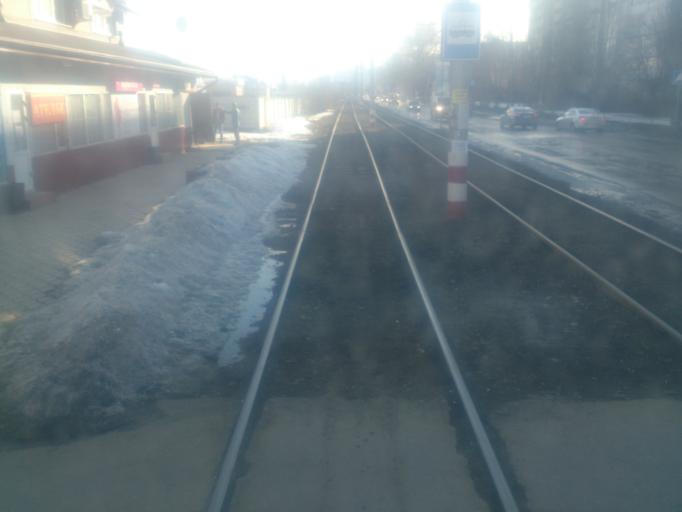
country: RU
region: Ulyanovsk
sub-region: Ulyanovskiy Rayon
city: Ulyanovsk
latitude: 54.2676
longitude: 48.2838
